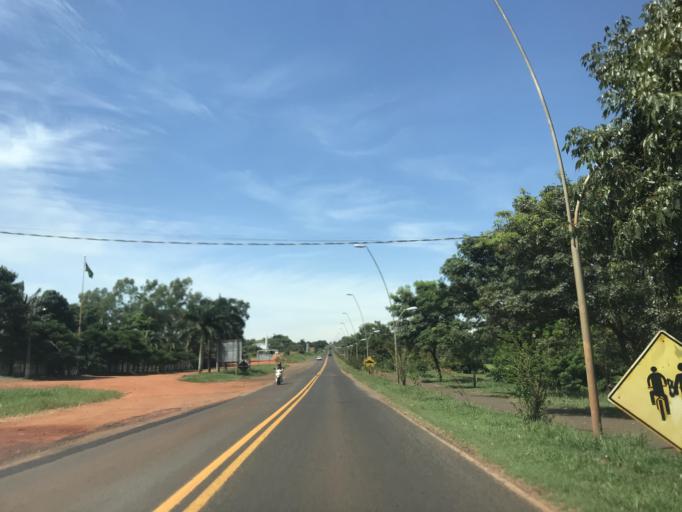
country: BR
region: Parana
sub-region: Terra Rica
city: Terra Rica
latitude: -22.7387
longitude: -52.6247
